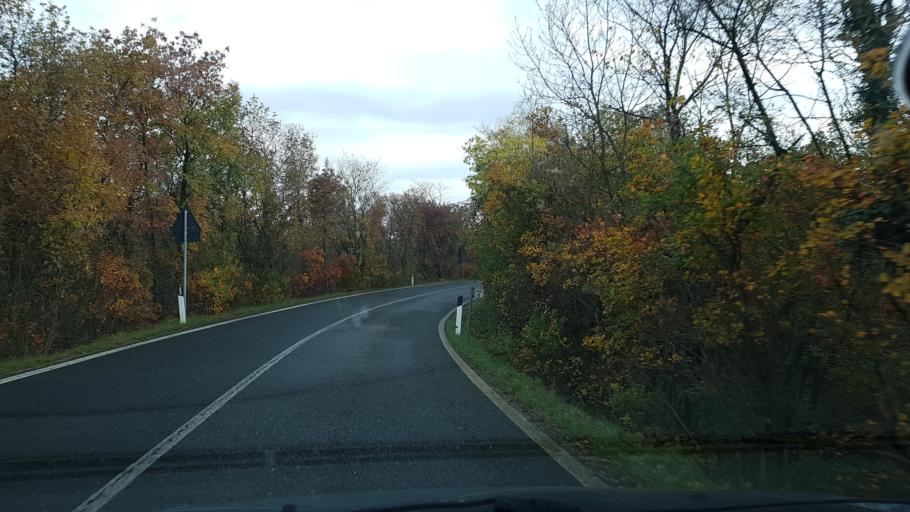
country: IT
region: Friuli Venezia Giulia
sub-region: Provincia di Gorizia
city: Doberdo del Lago
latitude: 45.8604
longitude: 13.5527
